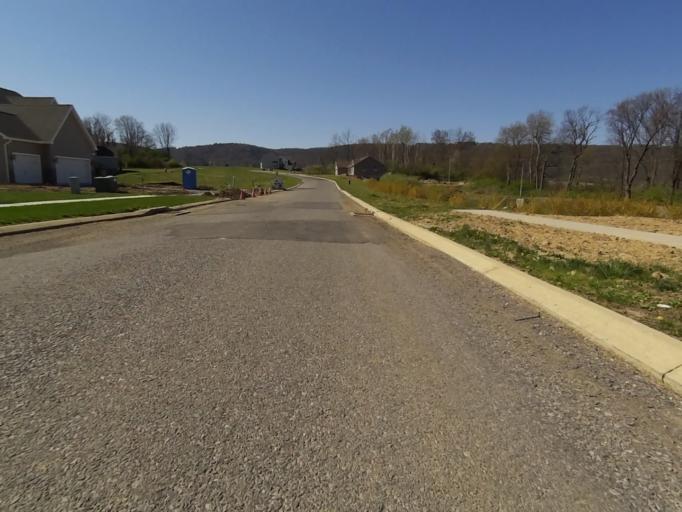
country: US
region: Pennsylvania
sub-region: Centre County
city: Houserville
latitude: 40.8797
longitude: -77.8300
